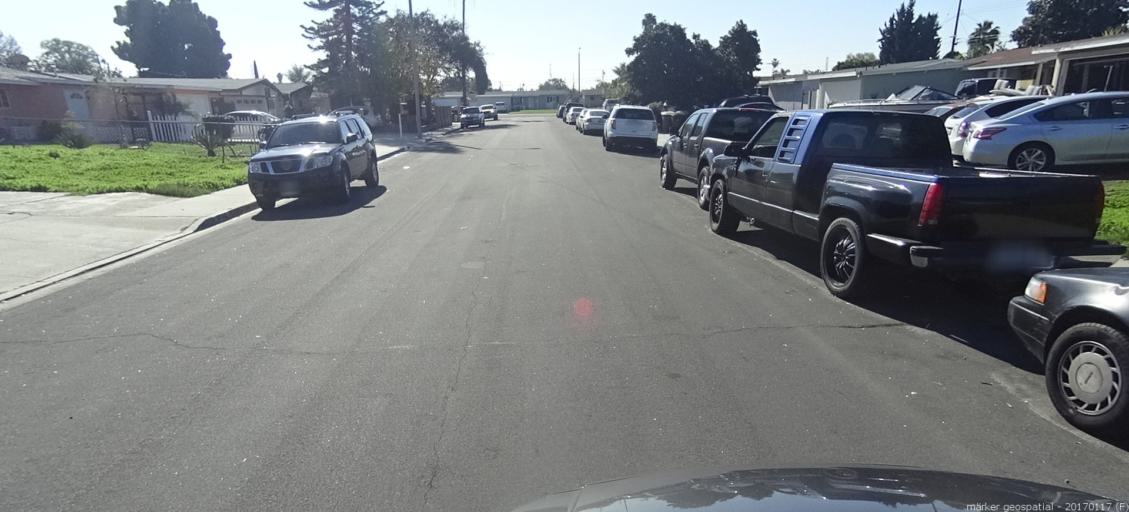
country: US
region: California
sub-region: Orange County
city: Stanton
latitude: 33.8154
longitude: -117.9608
